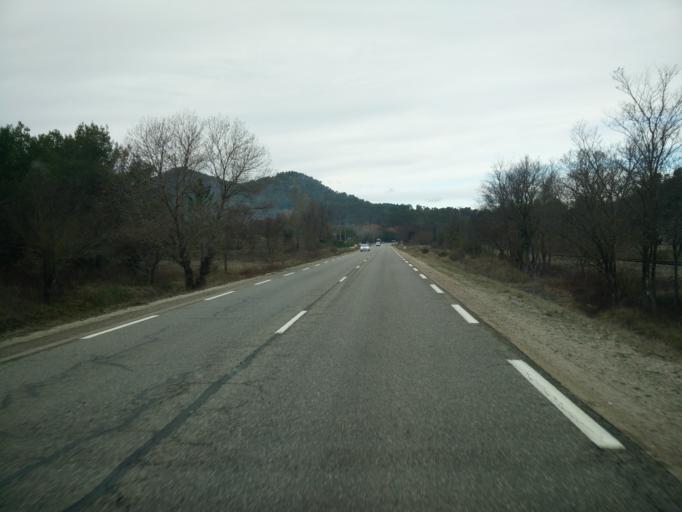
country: FR
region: Provence-Alpes-Cote d'Azur
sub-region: Departement du Var
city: La Celle
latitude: 43.3834
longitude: 6.0517
